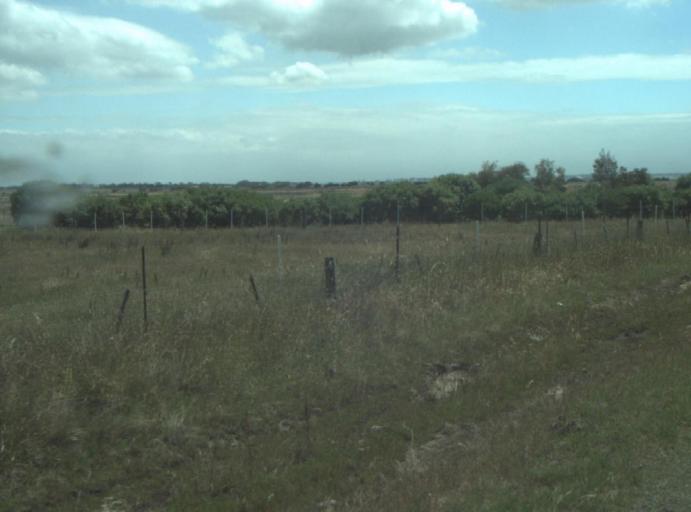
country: AU
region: Victoria
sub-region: Greater Geelong
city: Leopold
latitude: -38.2714
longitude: 144.4377
